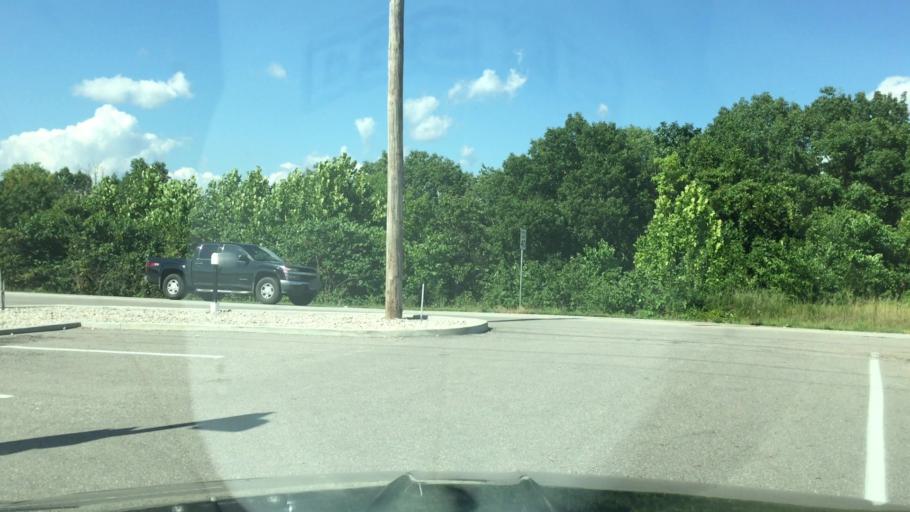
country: US
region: Missouri
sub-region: Miller County
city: Lake Ozark
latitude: 38.1774
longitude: -92.6198
